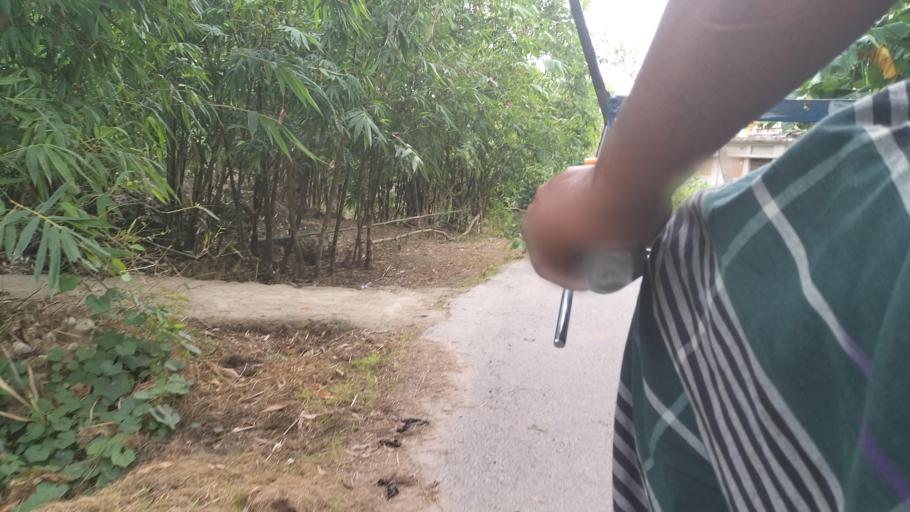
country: BD
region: Rajshahi
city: Rajshahi
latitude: 24.5495
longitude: 88.6048
